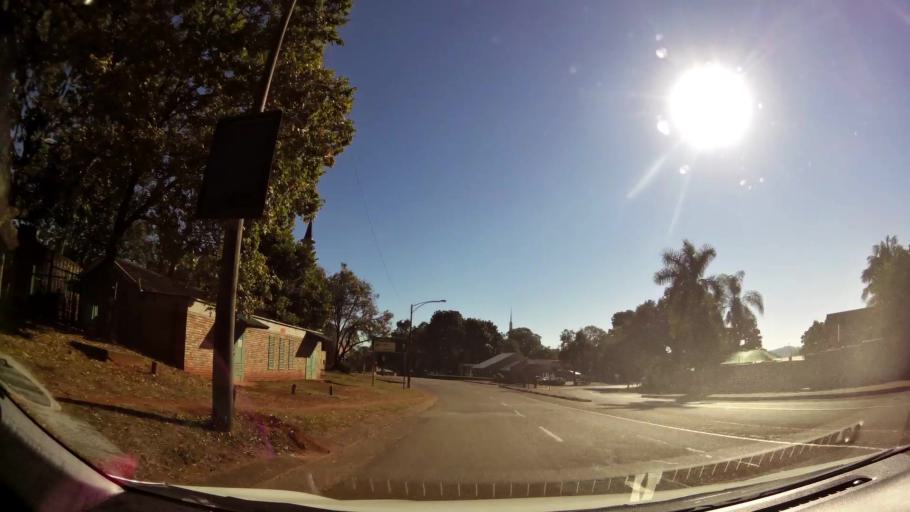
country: ZA
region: Limpopo
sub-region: Mopani District Municipality
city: Tzaneen
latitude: -23.8353
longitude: 30.1547
